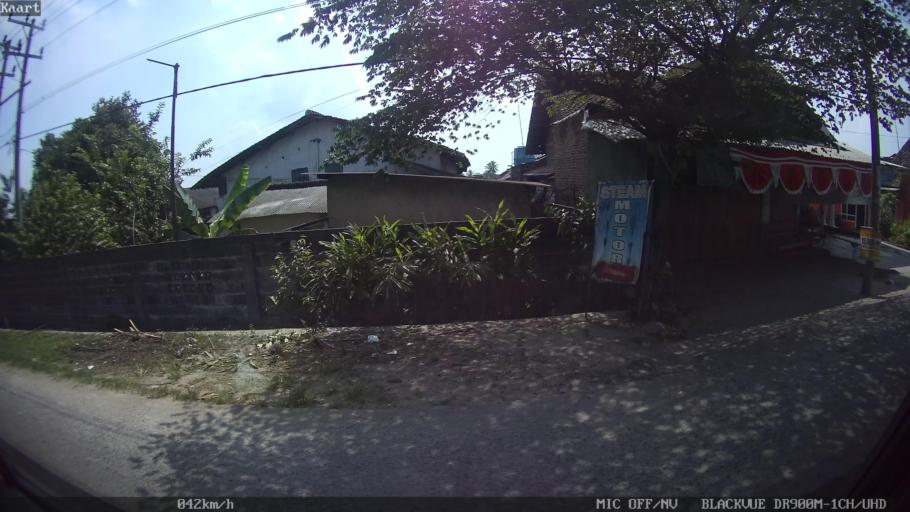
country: ID
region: Lampung
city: Natar
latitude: -5.2767
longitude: 105.1881
